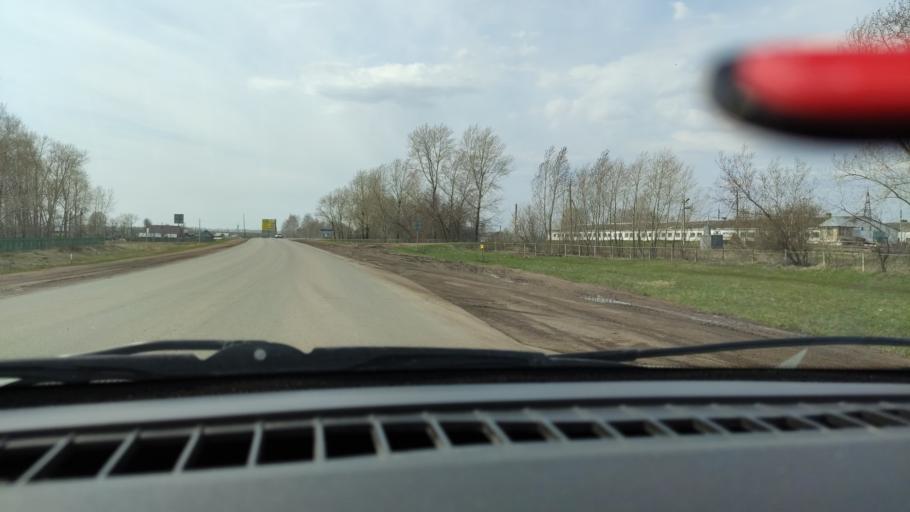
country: RU
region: Bashkortostan
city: Dyurtyuli
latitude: 55.4926
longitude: 54.8070
